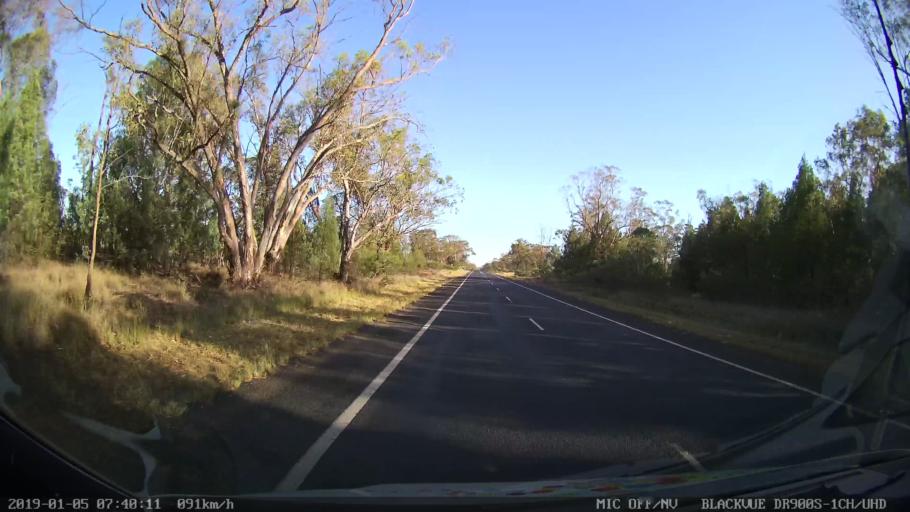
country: AU
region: New South Wales
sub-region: Gilgandra
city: Gilgandra
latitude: -31.9276
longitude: 148.6196
